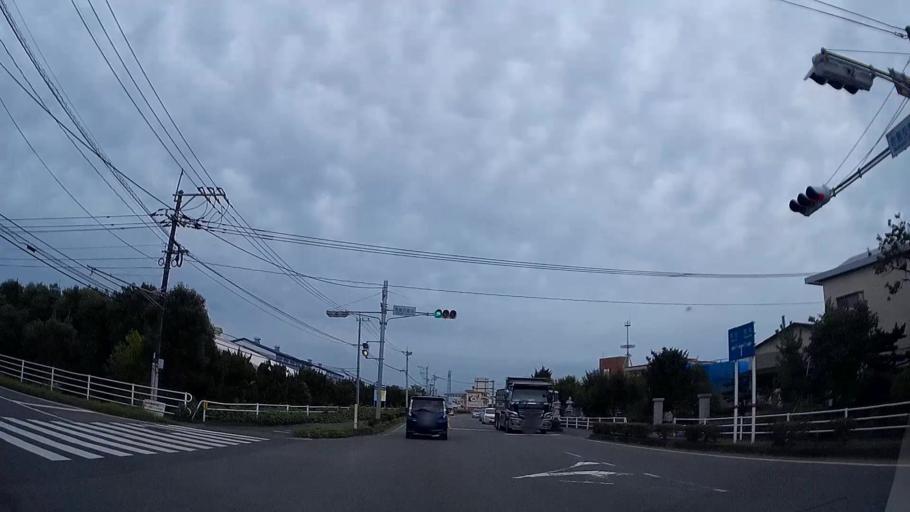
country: JP
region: Kumamoto
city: Kikuchi
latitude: 32.9602
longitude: 130.8178
